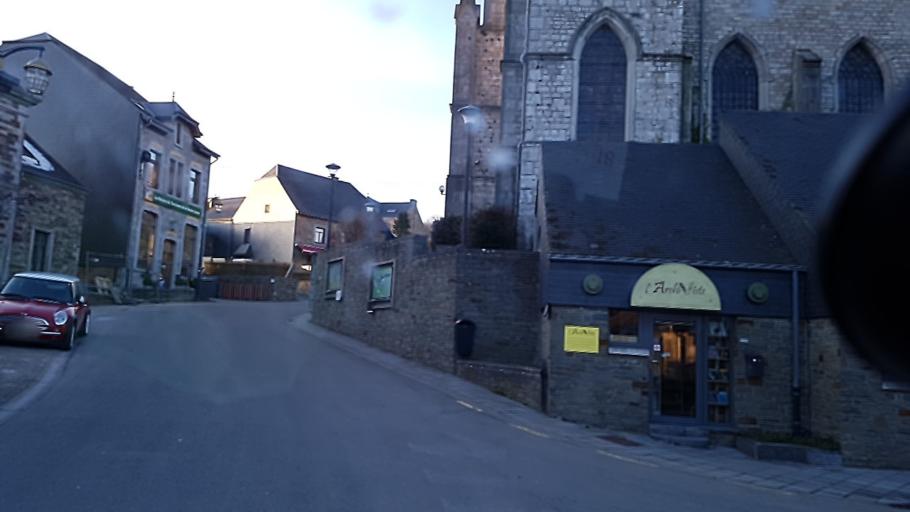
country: BE
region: Wallonia
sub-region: Province du Luxembourg
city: Daverdisse
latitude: 50.0069
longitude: 5.1604
